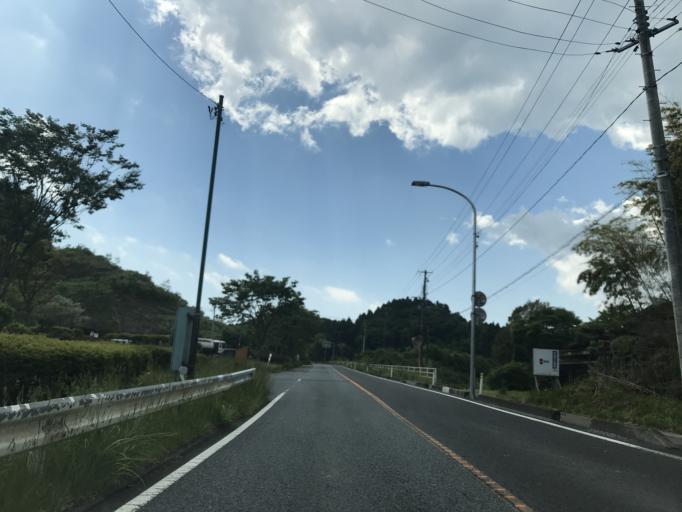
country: JP
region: Miyagi
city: Matsushima
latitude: 38.4205
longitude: 141.0590
